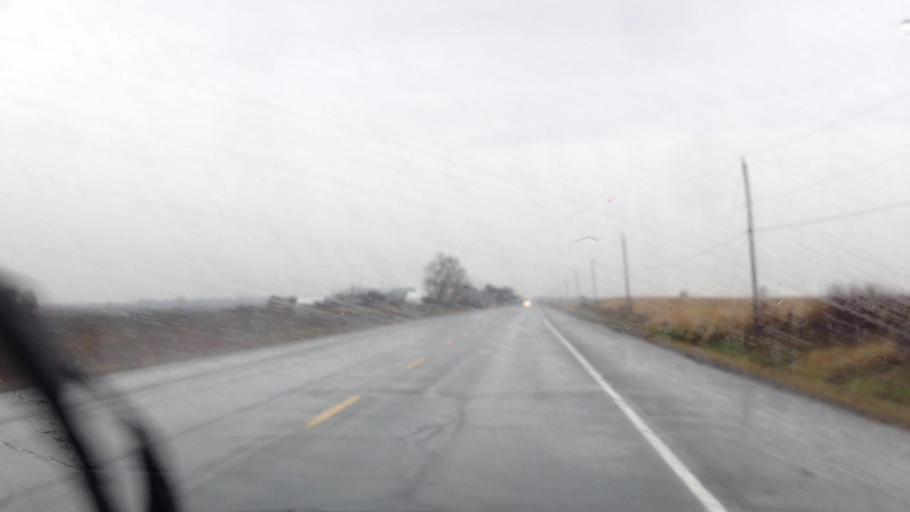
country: CA
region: Ontario
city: Clarence-Rockland
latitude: 45.4648
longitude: -75.4321
